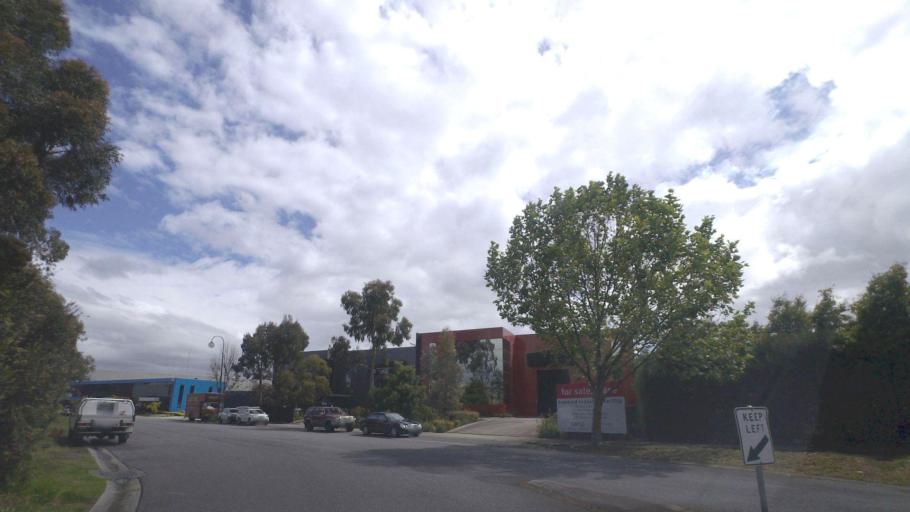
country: AU
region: Victoria
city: Forest Hill
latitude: -37.8302
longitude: 145.1893
